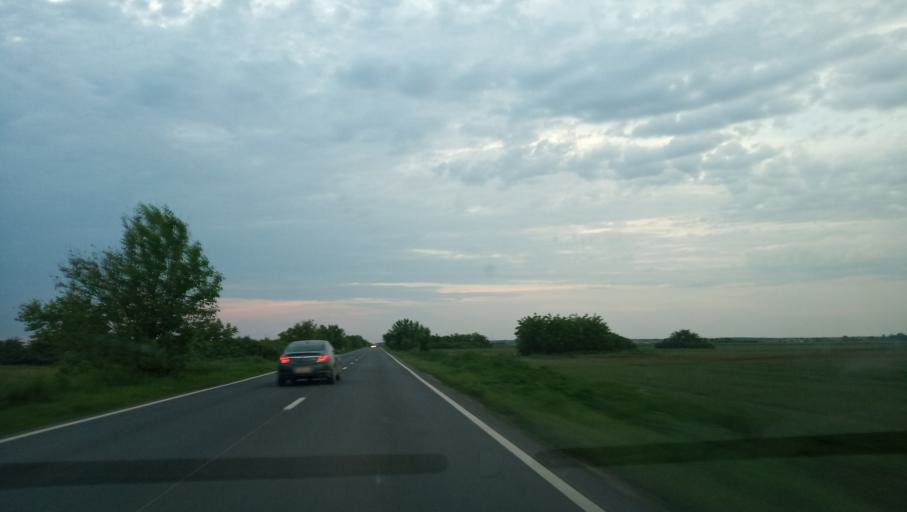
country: RO
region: Timis
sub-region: Comuna Padureni
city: Padureni
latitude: 45.5808
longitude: 21.2020
